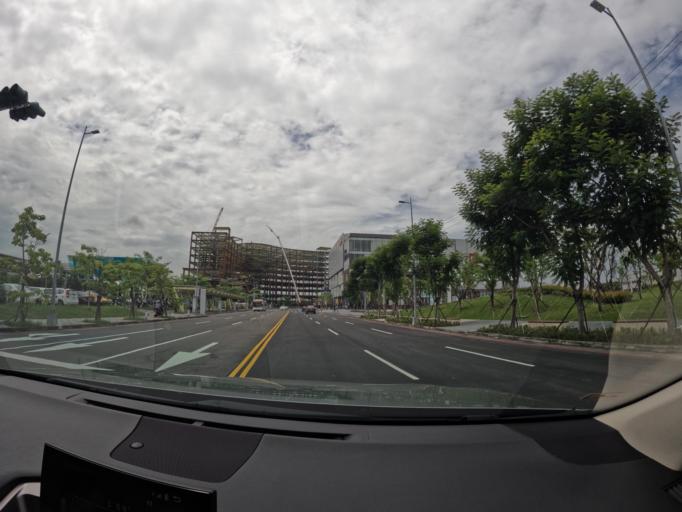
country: TW
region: Kaohsiung
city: Kaohsiung
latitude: 22.7811
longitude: 120.3003
